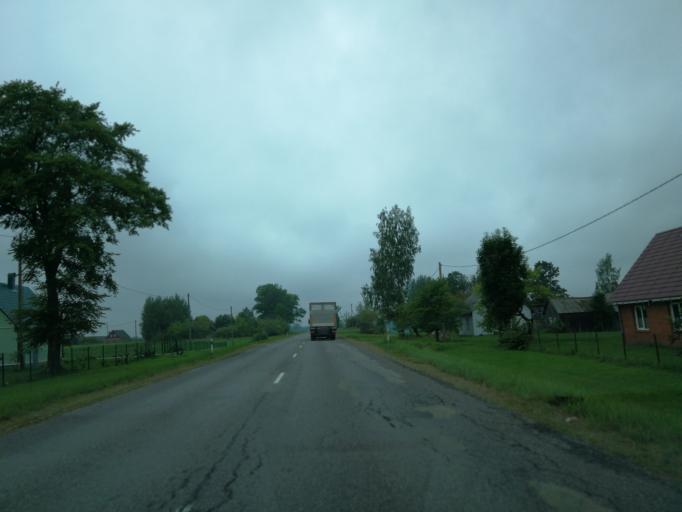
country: LV
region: Livani
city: Livani
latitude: 56.3469
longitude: 26.2915
